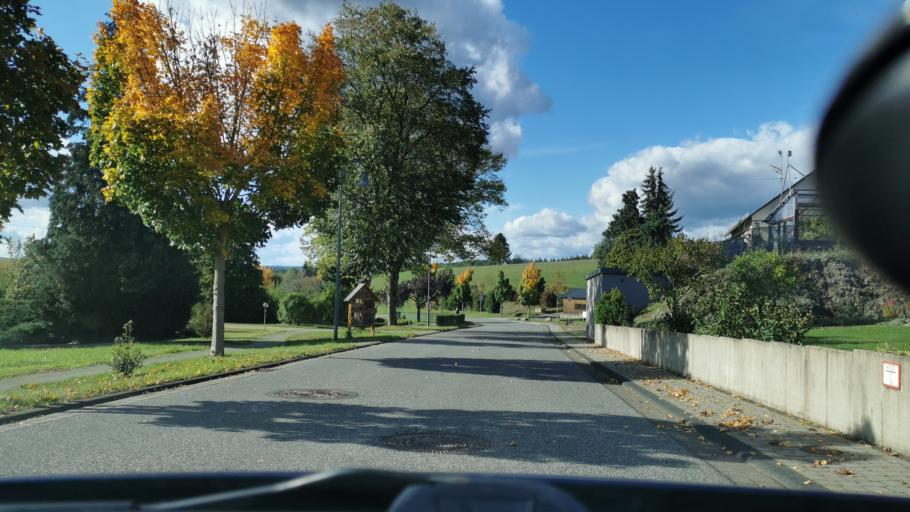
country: DE
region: Rheinland-Pfalz
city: Hupperath
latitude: 49.9969
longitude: 6.8313
